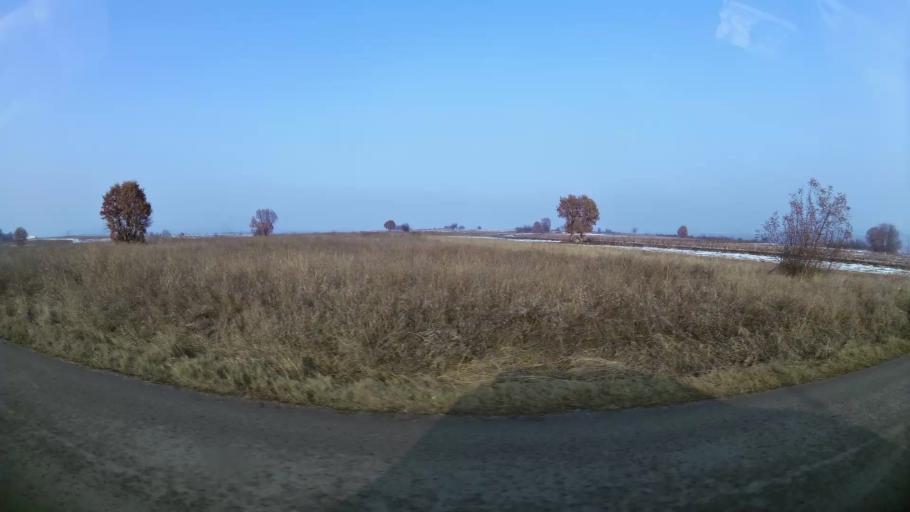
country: MK
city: Miladinovci
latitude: 41.9729
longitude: 21.6337
